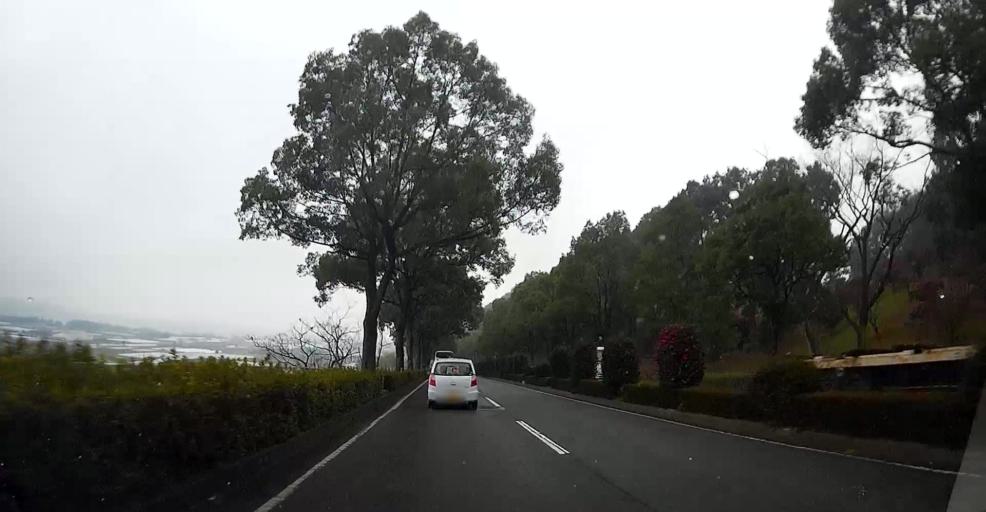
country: JP
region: Kumamoto
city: Ozu
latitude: 32.8200
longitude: 130.8469
